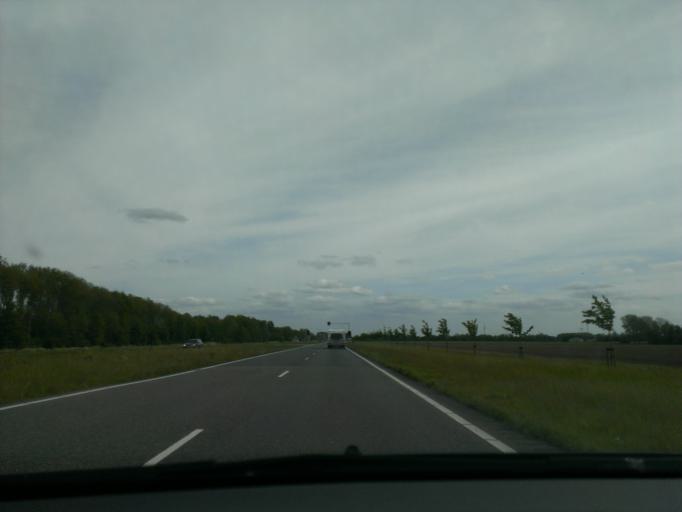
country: NL
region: Flevoland
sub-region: Gemeente Lelystad
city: Lelystad
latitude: 52.4484
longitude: 5.5478
